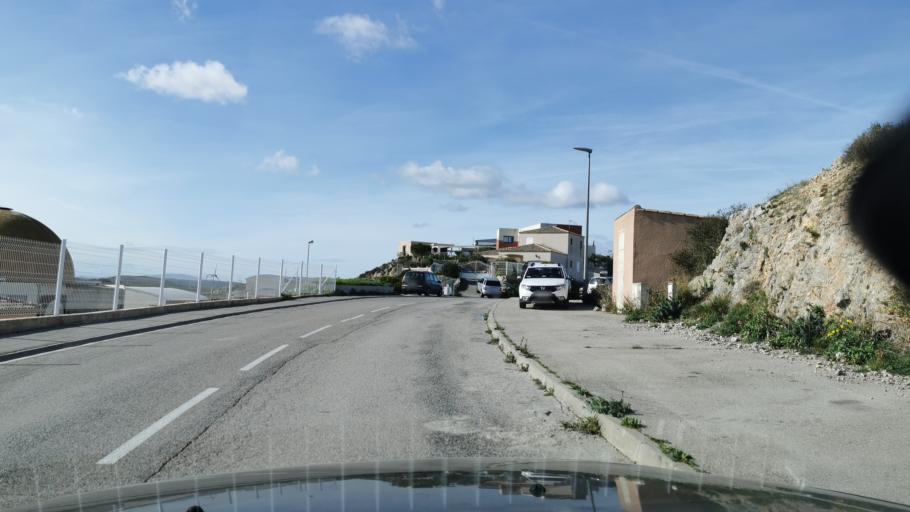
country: FR
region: Languedoc-Roussillon
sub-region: Departement de l'Aude
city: Narbonne
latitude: 43.1641
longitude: 2.9708
